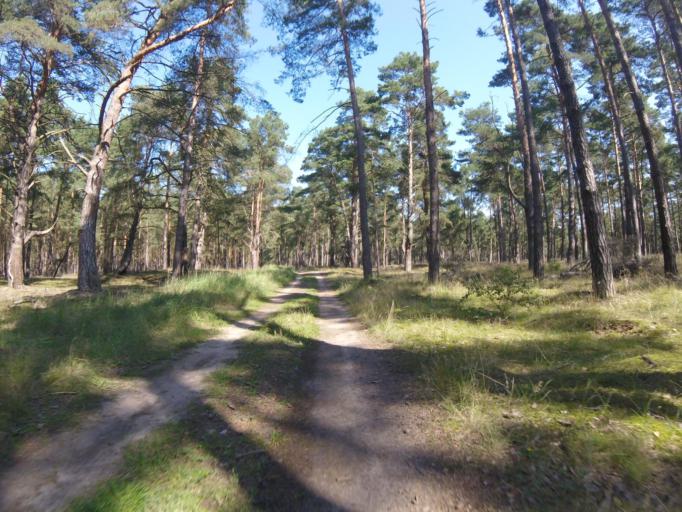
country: DE
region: Brandenburg
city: Mittenwalde
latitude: 52.2208
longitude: 13.5897
